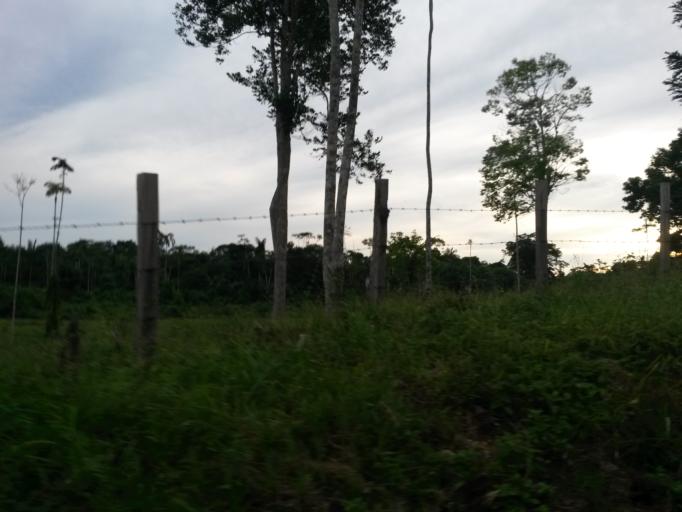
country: CO
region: Caqueta
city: Curillo
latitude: 1.1291
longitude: -76.2476
